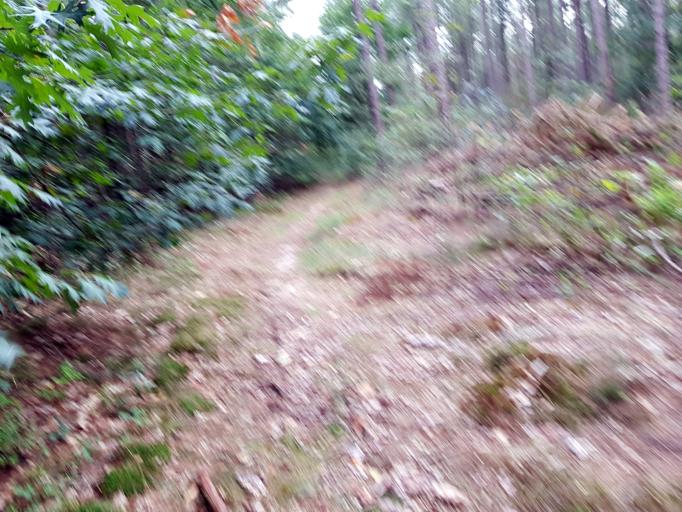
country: NL
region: Utrecht
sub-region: Gemeente Utrechtse Heuvelrug
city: Amerongen
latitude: 52.0164
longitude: 5.4487
